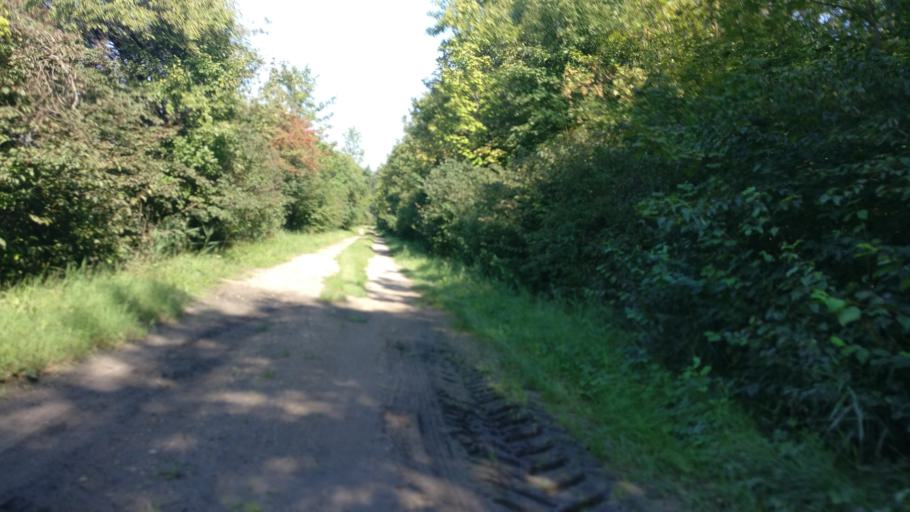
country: AT
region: Lower Austria
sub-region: Politischer Bezirk Baden
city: Ebreichsdorf
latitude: 47.9927
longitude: 16.4007
